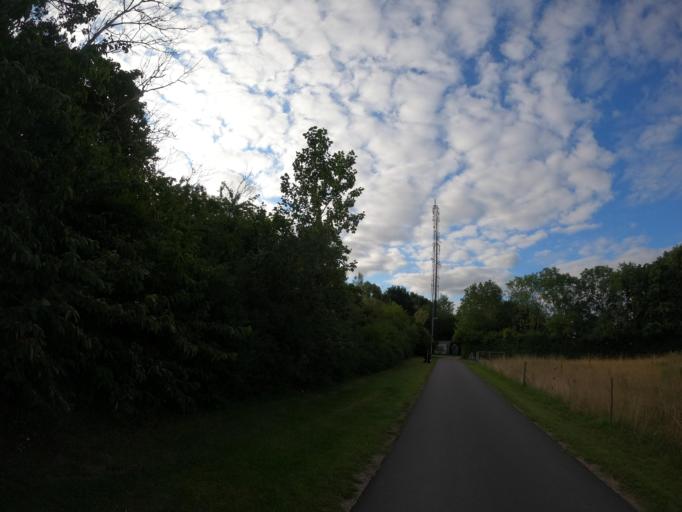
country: SE
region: Skane
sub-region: Staffanstorps Kommun
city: Staffanstorp
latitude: 55.6561
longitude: 13.2132
